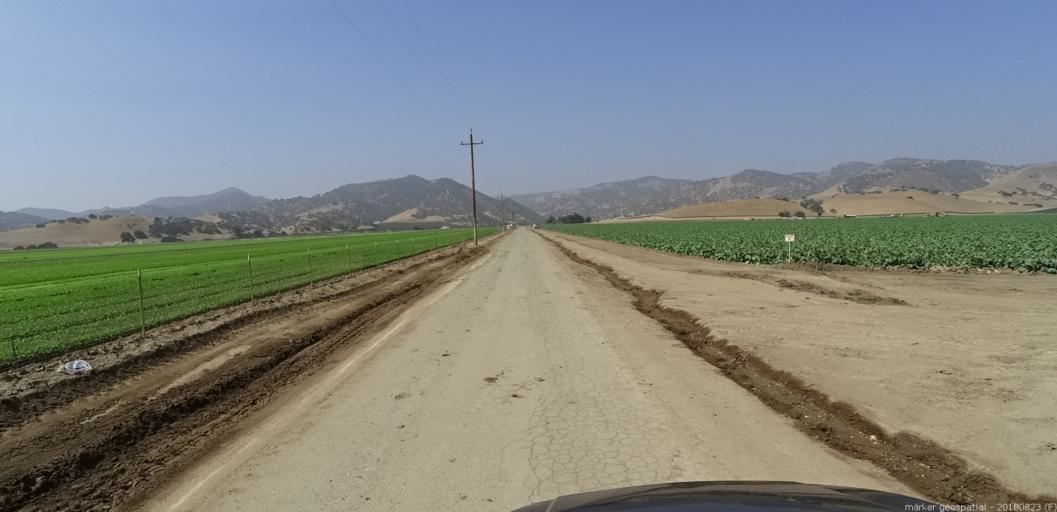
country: US
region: California
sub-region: Monterey County
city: King City
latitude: 36.2313
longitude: -121.1768
